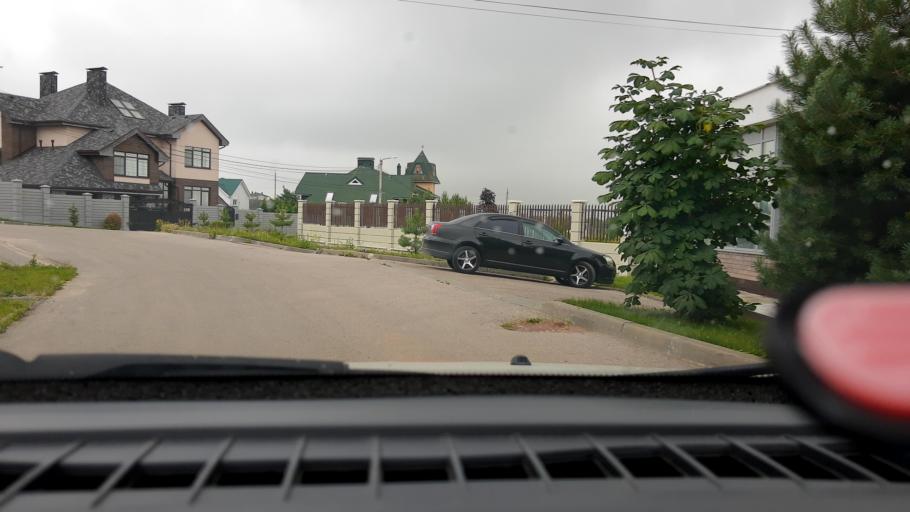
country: RU
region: Nizjnij Novgorod
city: Afonino
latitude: 56.2801
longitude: 44.0707
